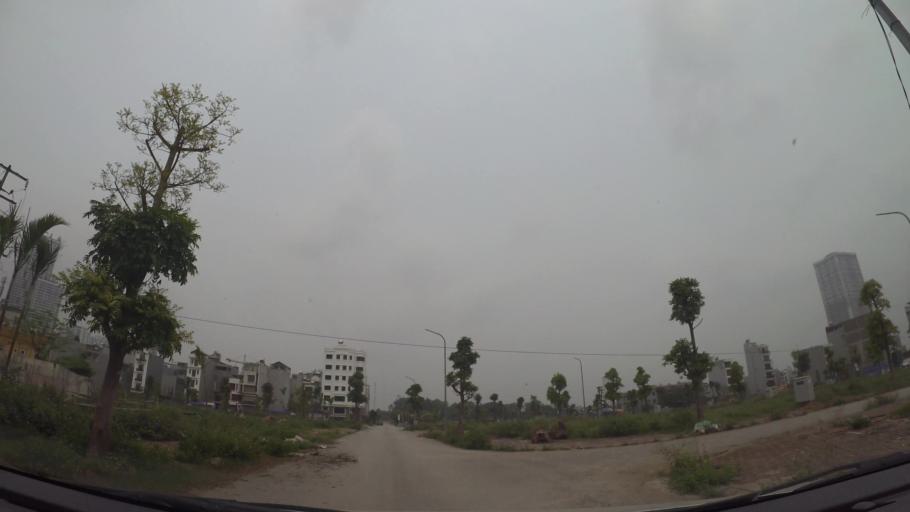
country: VN
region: Ha Noi
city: Ha Dong
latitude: 20.9755
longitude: 105.7684
